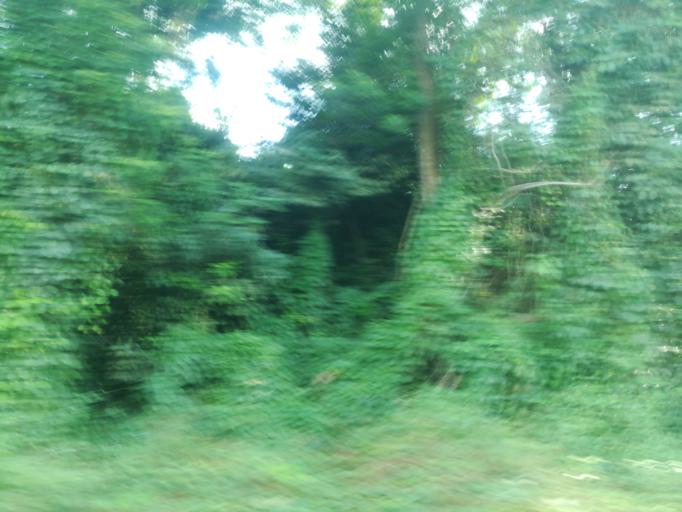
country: NG
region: Oyo
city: Ido
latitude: 7.3959
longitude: 3.7867
